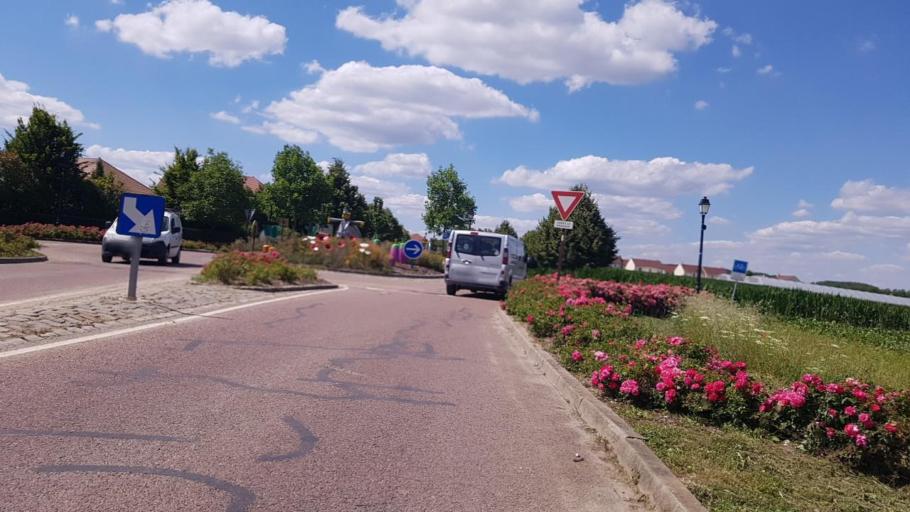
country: FR
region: Ile-de-France
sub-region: Departement de Seine-et-Marne
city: Moussy-le-Neuf
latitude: 49.0588
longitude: 2.6114
